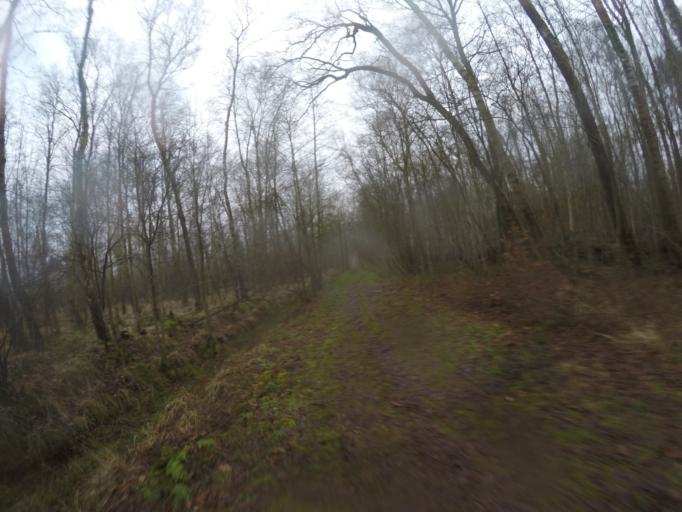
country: DE
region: Schleswig-Holstein
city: Quickborn
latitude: 53.7170
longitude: 9.9261
